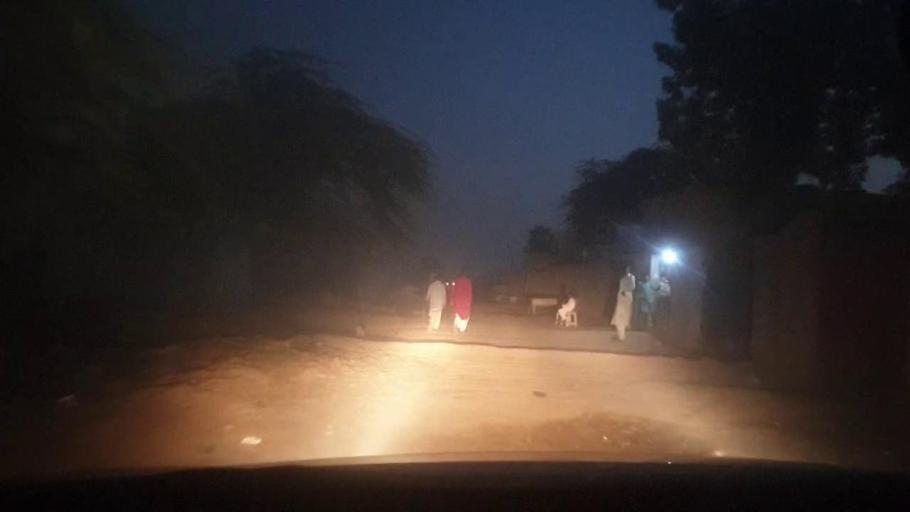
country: PK
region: Sindh
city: Tando Mittha Khan
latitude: 25.8075
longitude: 69.3625
